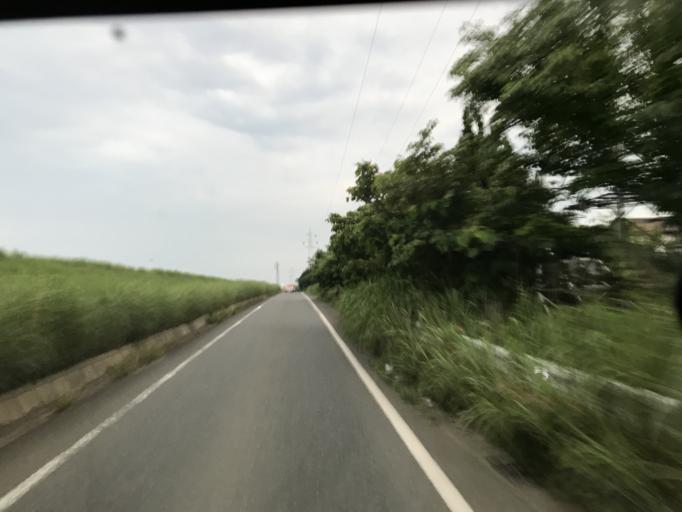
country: JP
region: Ibaraki
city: Ryugasaki
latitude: 35.8409
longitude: 140.1514
